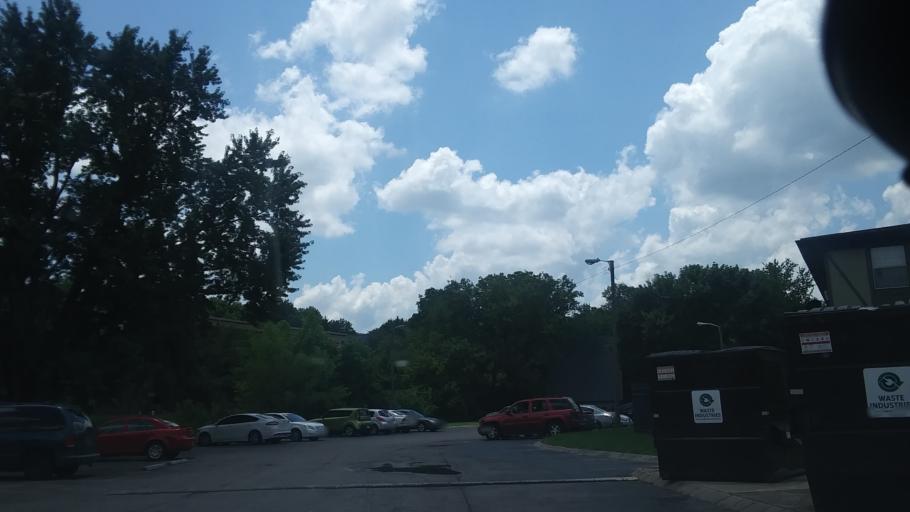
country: US
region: Tennessee
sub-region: Davidson County
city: Oak Hill
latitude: 36.0800
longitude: -86.6991
